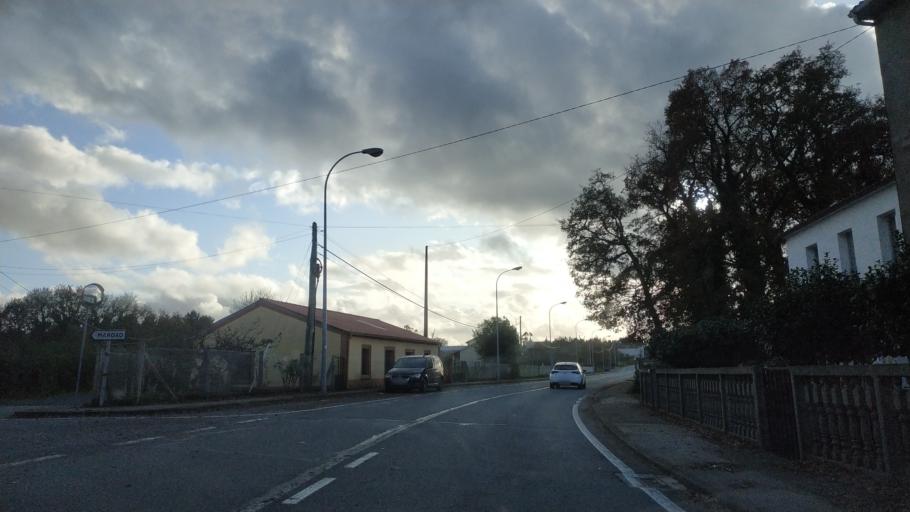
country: ES
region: Galicia
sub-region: Provincia da Coruna
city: Arzua
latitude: 42.9191
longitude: -8.1653
